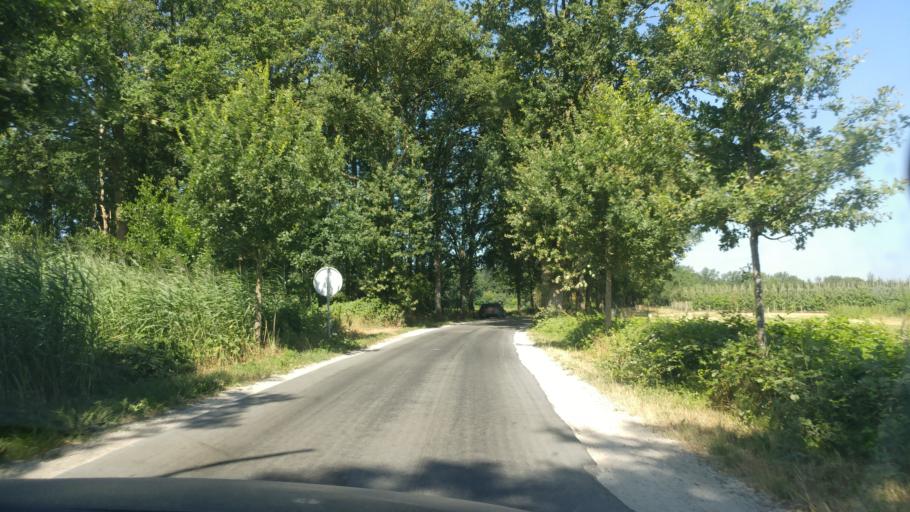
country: NL
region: North Brabant
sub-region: Gemeente Boxtel
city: Boxtel
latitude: 51.5690
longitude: 5.3034
